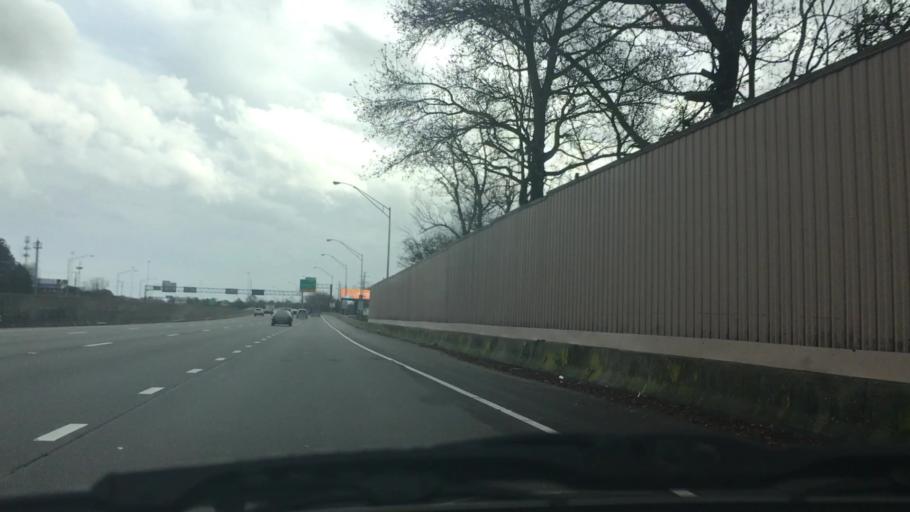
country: US
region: Virginia
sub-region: City of Norfolk
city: Norfolk
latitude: 36.9152
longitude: -76.2622
